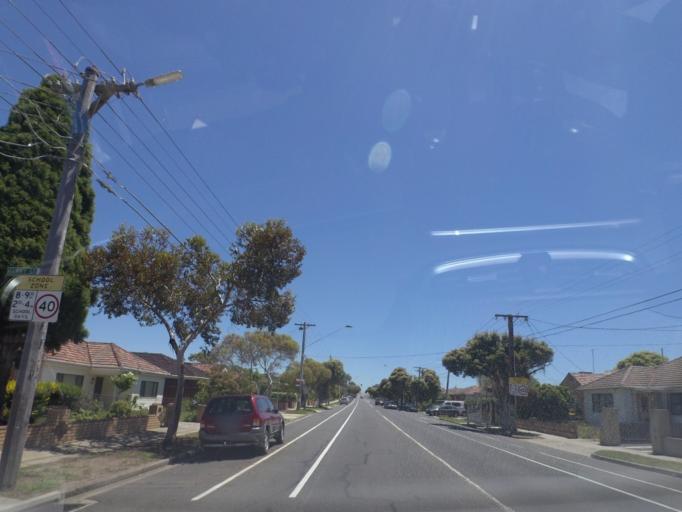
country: AU
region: Victoria
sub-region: Darebin
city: Preston
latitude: -37.7540
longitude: 145.0163
